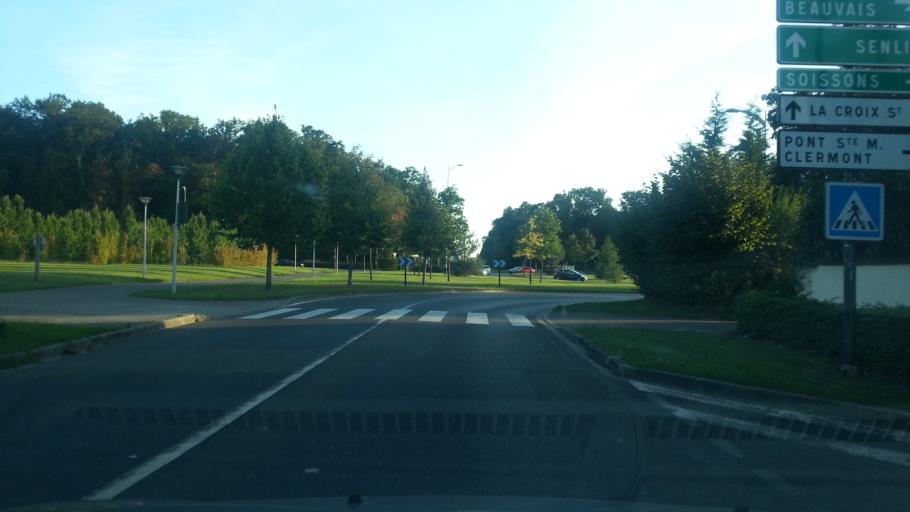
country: FR
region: Picardie
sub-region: Departement de l'Oise
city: Venette
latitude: 49.3938
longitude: 2.8032
